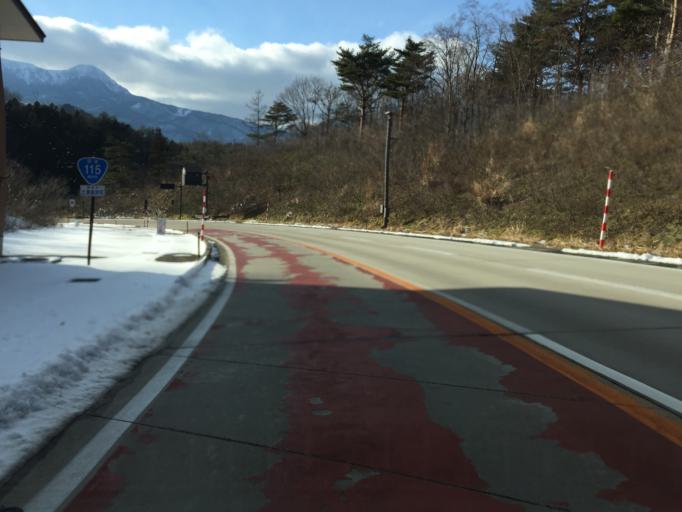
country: JP
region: Fukushima
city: Nihommatsu
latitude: 37.6808
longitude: 140.3378
